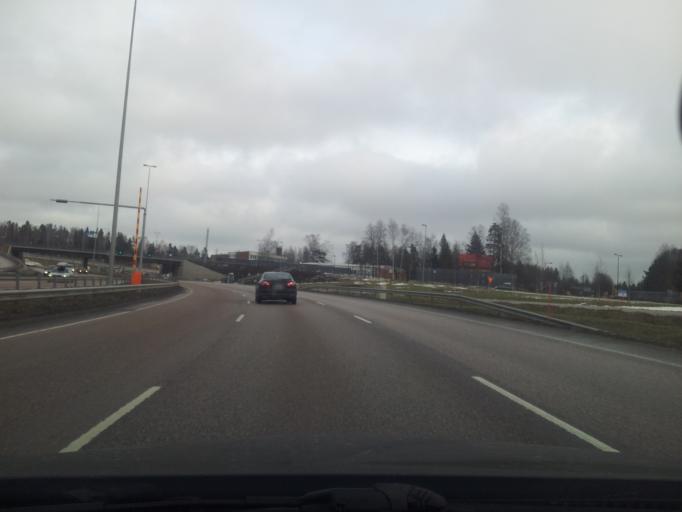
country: FI
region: Uusimaa
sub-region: Helsinki
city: Teekkarikylae
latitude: 60.2252
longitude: 24.8238
